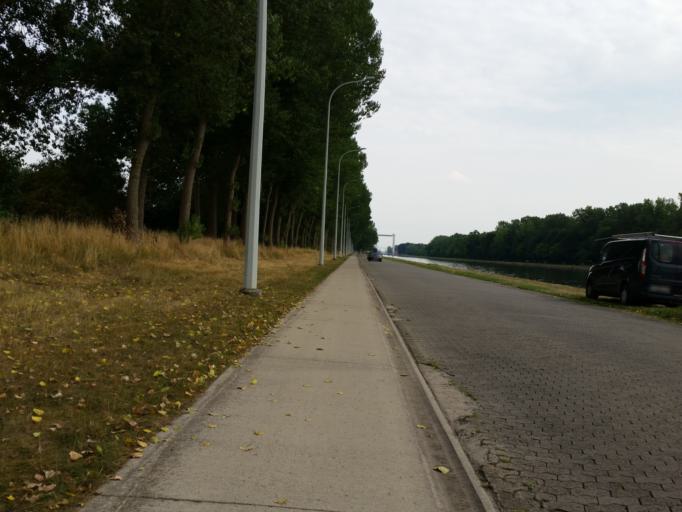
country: BE
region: Flanders
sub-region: Provincie Vlaams-Brabant
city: Kapelle-op-den-Bos
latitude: 50.9928
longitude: 4.3794
